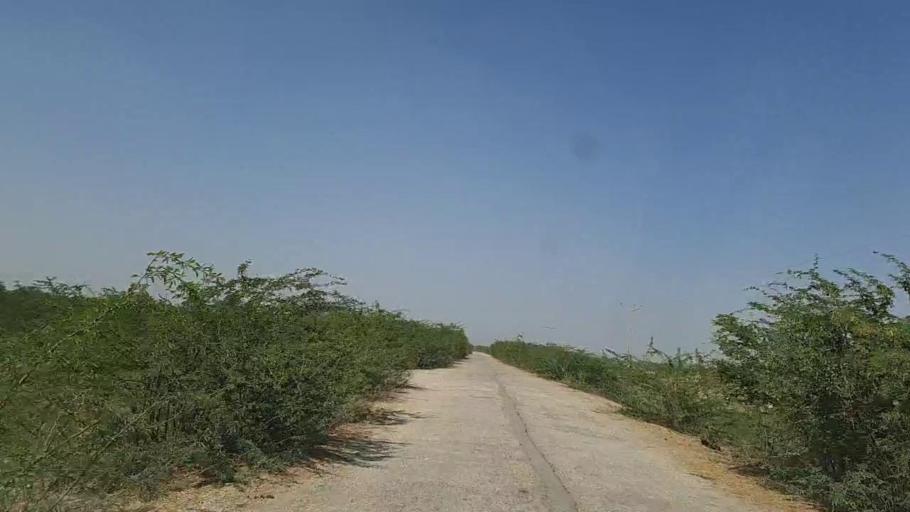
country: PK
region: Sindh
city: Naukot
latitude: 24.6340
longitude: 69.2882
